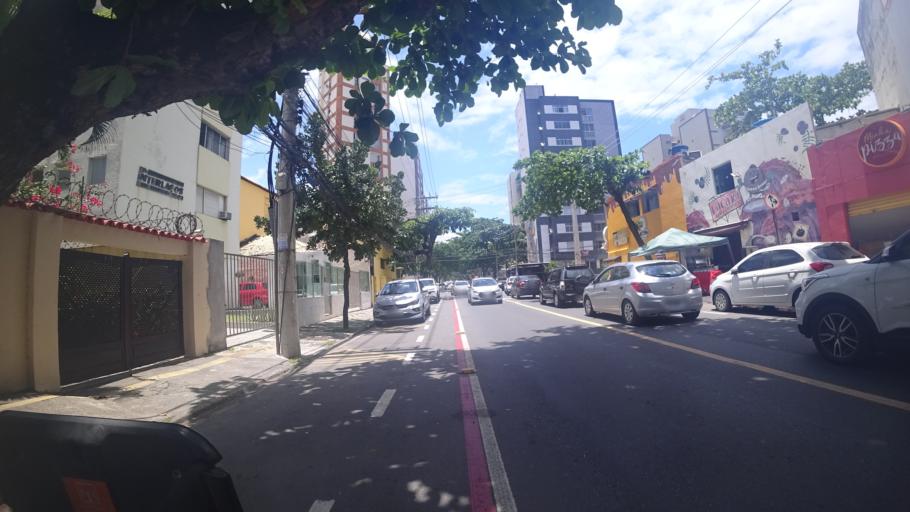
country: BR
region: Bahia
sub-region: Salvador
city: Salvador
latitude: -13.0058
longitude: -38.4622
